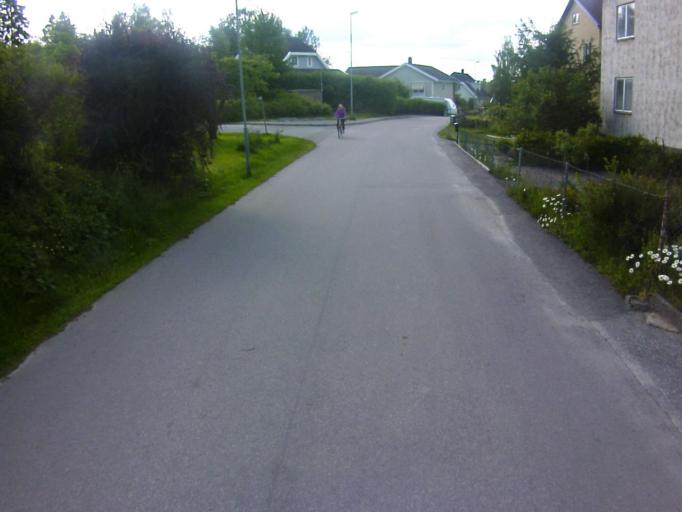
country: SE
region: Soedermanland
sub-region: Eskilstuna Kommun
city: Skogstorp
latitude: 59.3266
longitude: 16.4873
